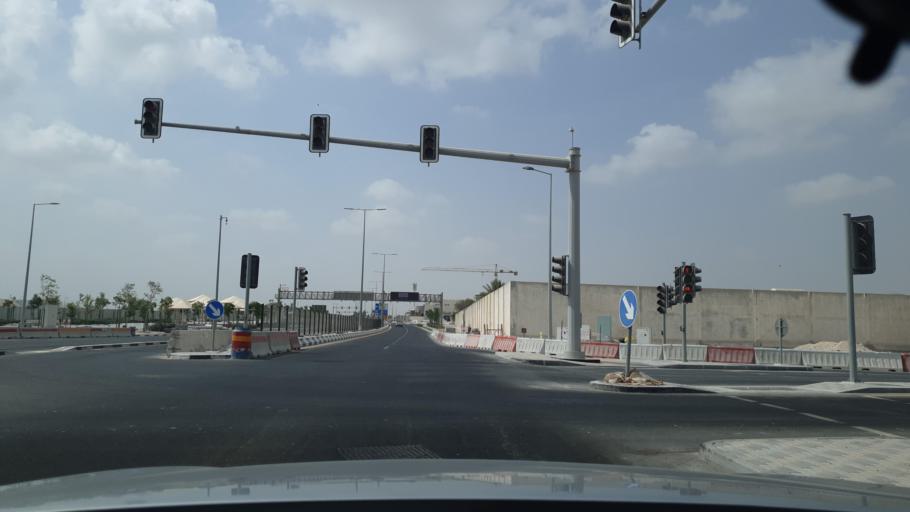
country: QA
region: Baladiyat ar Rayyan
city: Ar Rayyan
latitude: 25.2784
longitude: 51.4668
